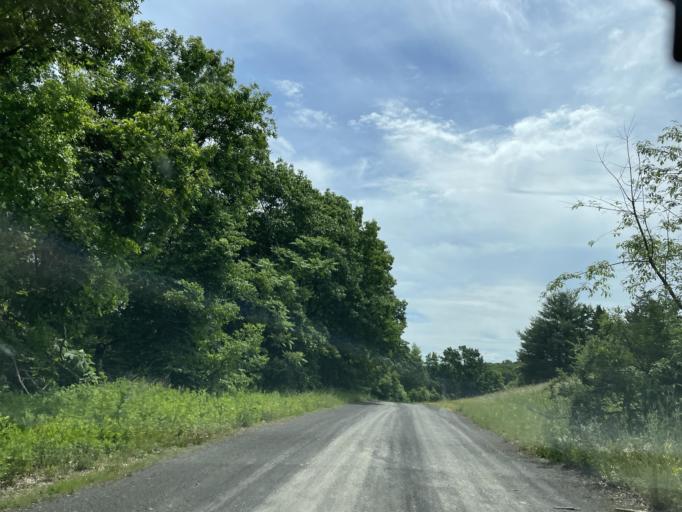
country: US
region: New York
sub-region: Ulster County
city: Lincoln Park
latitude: 41.9646
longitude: -74.0250
